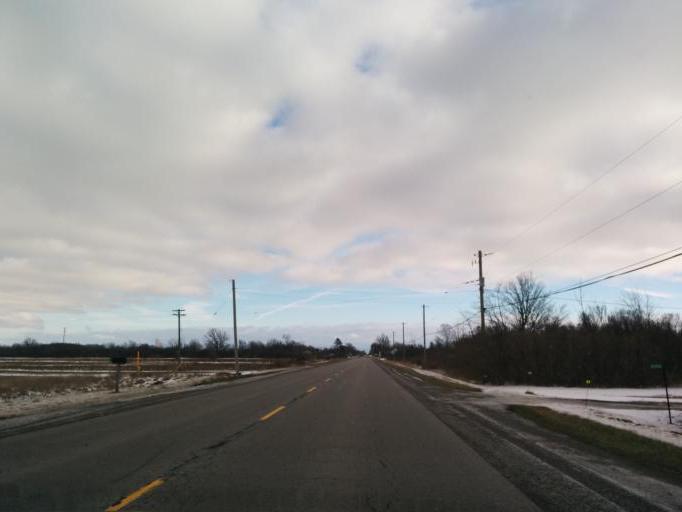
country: CA
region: Ontario
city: Brantford
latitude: 42.9694
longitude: -80.0717
